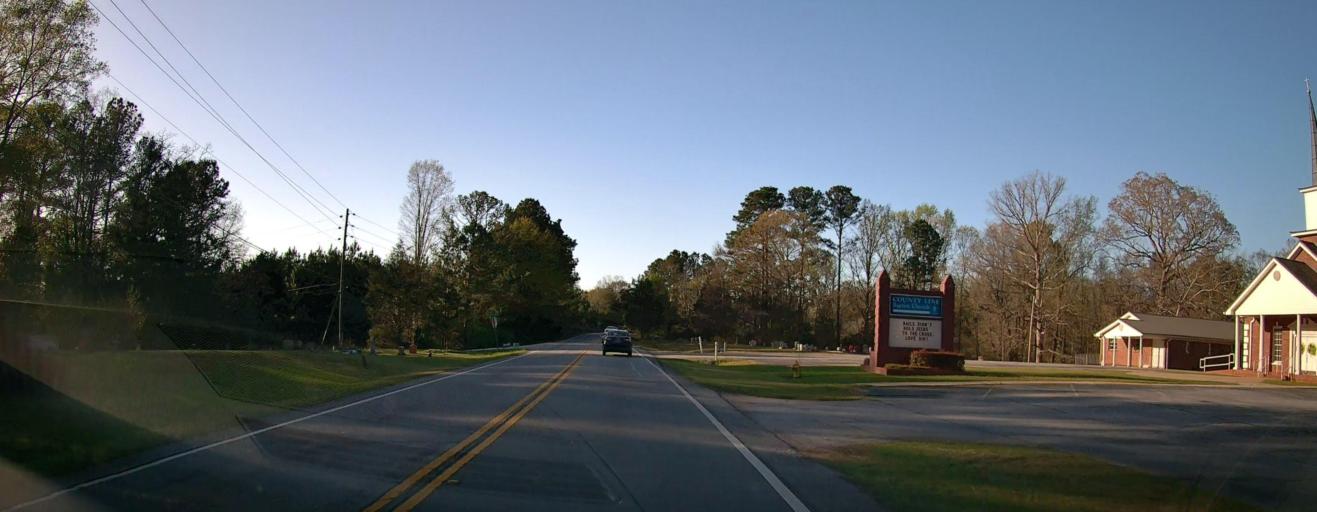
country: US
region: Georgia
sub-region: Newton County
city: Oakwood
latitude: 33.4812
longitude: -83.9149
